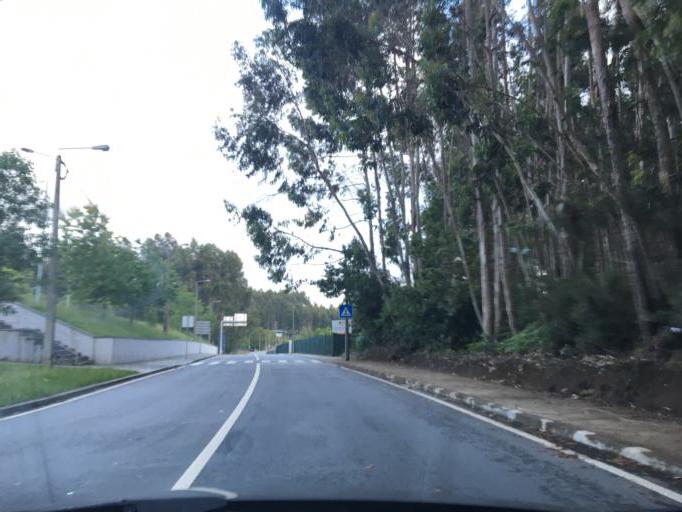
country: PT
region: Porto
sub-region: Maia
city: Gemunde
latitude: 41.2541
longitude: -8.6414
